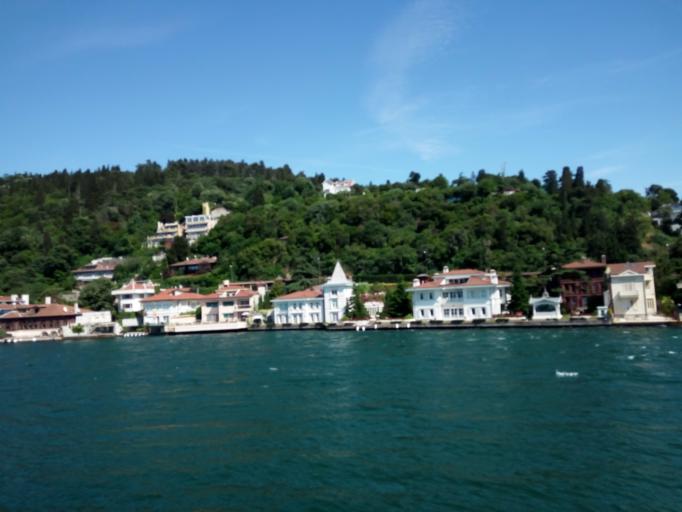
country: TR
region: Istanbul
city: UEskuedar
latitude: 41.0630
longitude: 29.0521
